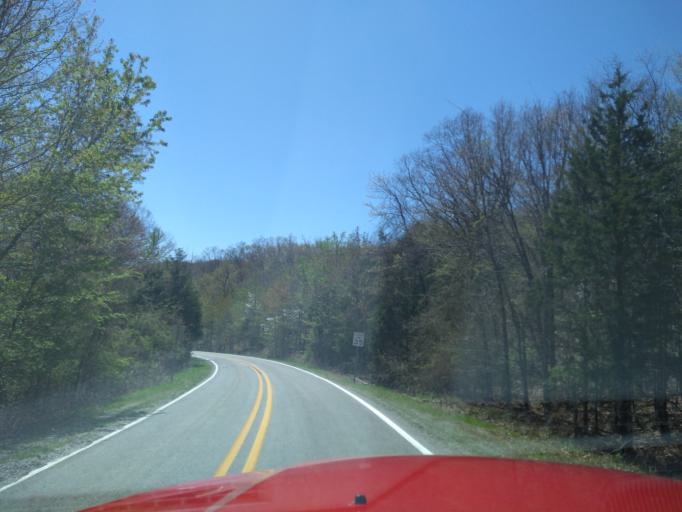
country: US
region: Arkansas
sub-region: Washington County
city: West Fork
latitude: 35.7908
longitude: -94.2556
